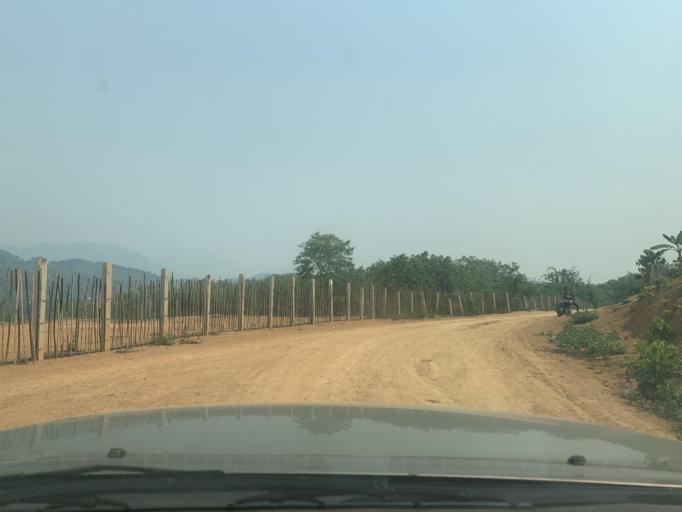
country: LA
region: Louangphabang
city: Xiang Ngeun
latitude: 19.7990
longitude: 102.2014
